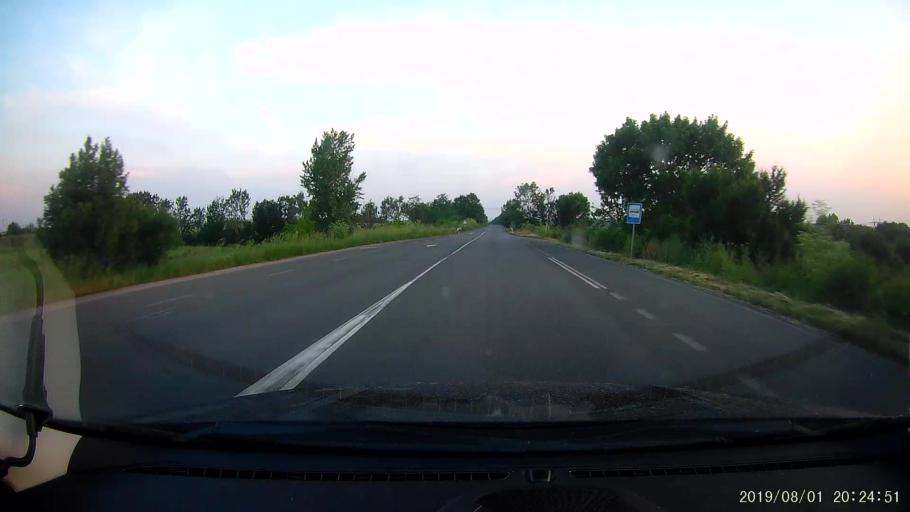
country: BG
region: Yambol
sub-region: Obshtina Elkhovo
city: Elkhovo
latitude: 42.2252
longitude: 26.5911
